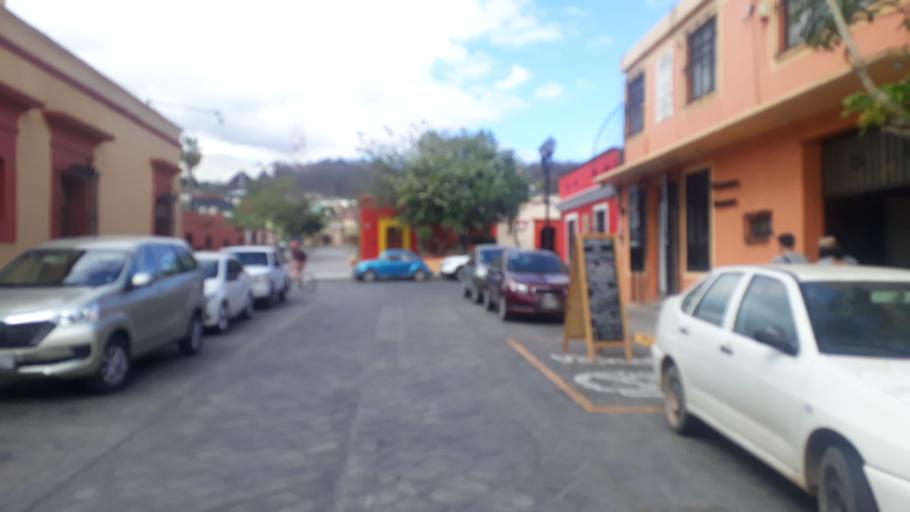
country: MX
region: Oaxaca
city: Oaxaca de Juarez
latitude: 17.0696
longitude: -96.7228
